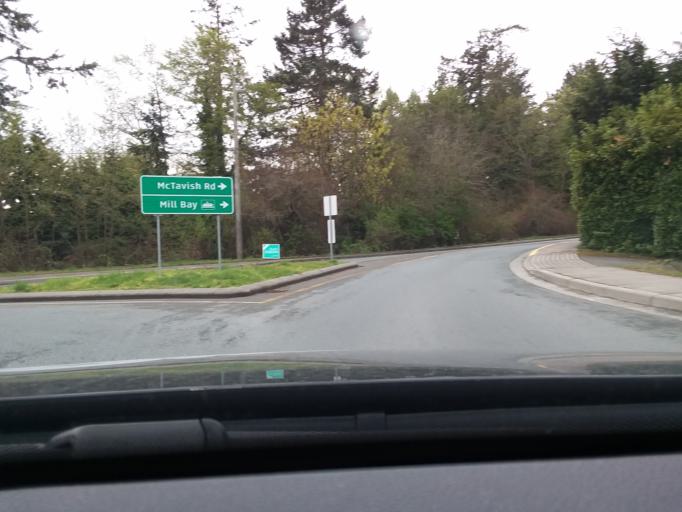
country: CA
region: British Columbia
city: North Saanich
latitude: 48.6303
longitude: -123.4141
